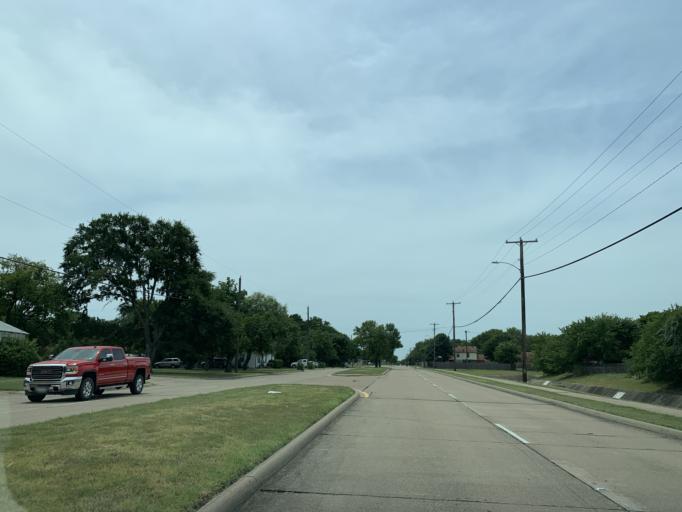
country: US
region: Texas
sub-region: Dallas County
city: Cedar Hill
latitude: 32.6542
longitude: -97.0150
